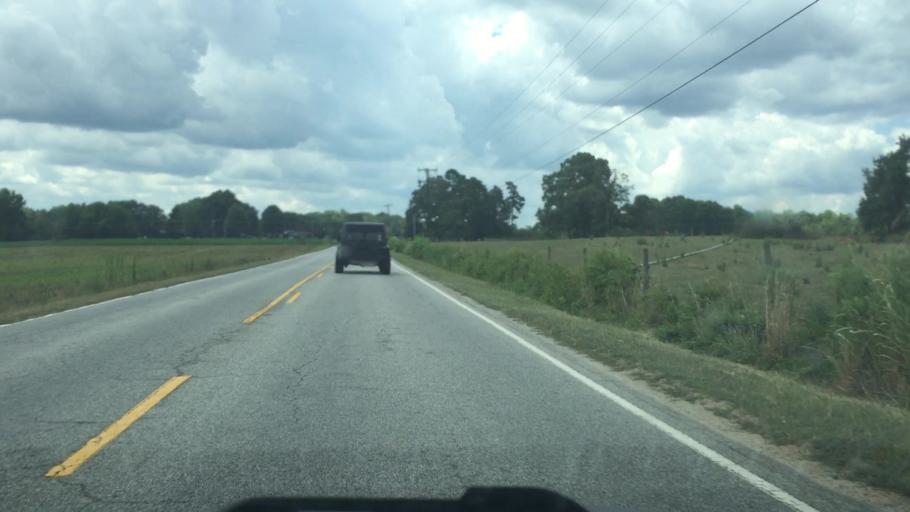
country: US
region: North Carolina
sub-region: Rowan County
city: Enochville
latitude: 35.5744
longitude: -80.6545
